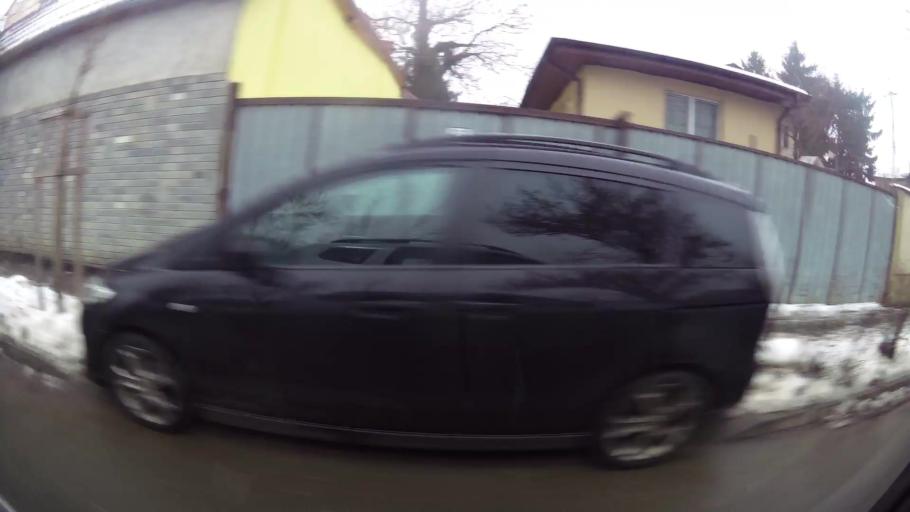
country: RO
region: Ilfov
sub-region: Comuna Chiajna
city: Rosu
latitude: 44.4456
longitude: 26.0314
